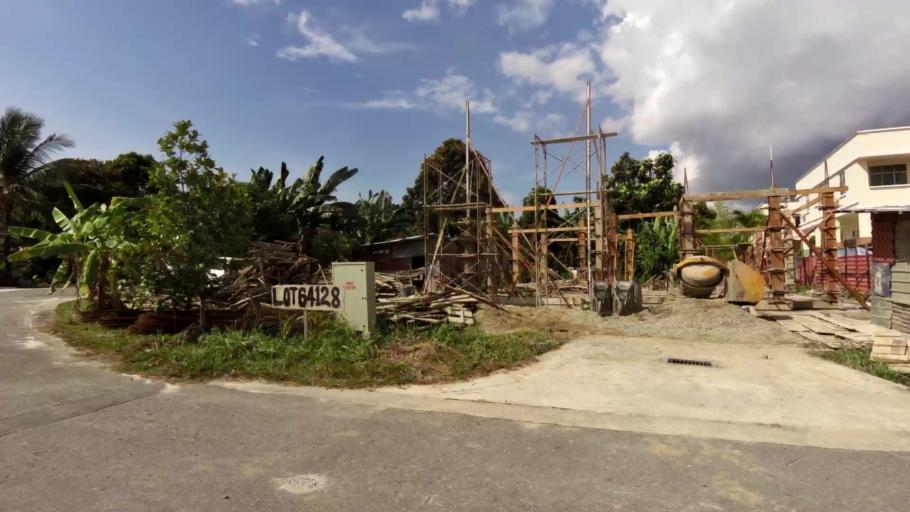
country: BN
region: Brunei and Muara
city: Bandar Seri Begawan
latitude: 4.9536
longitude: 114.9532
